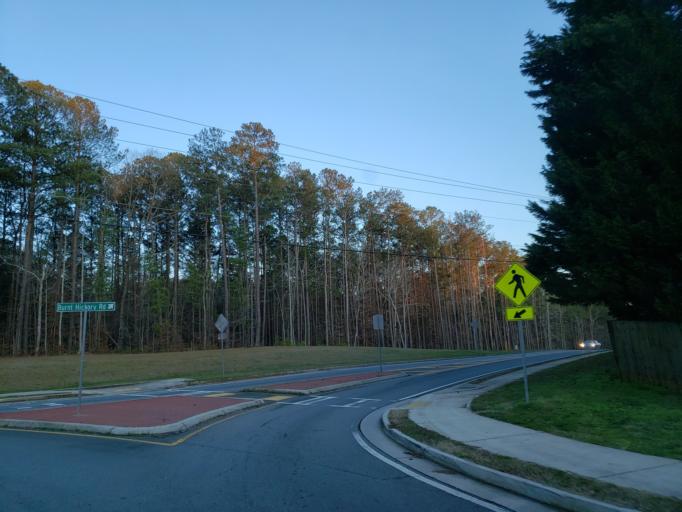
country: US
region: Georgia
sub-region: Cobb County
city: Acworth
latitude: 33.9982
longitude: -84.7291
